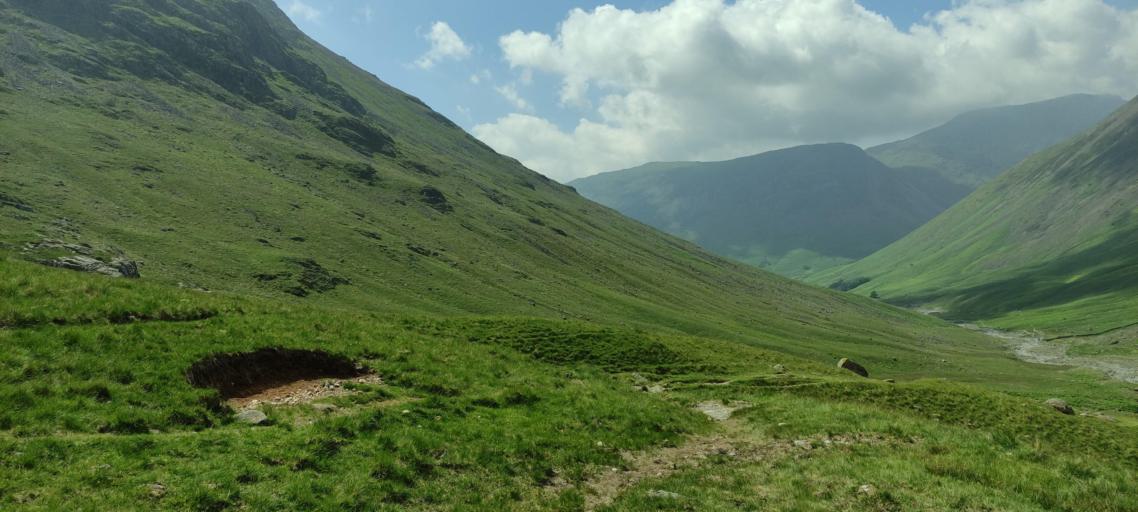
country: GB
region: England
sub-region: Cumbria
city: Keswick
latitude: 54.4709
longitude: -3.2135
